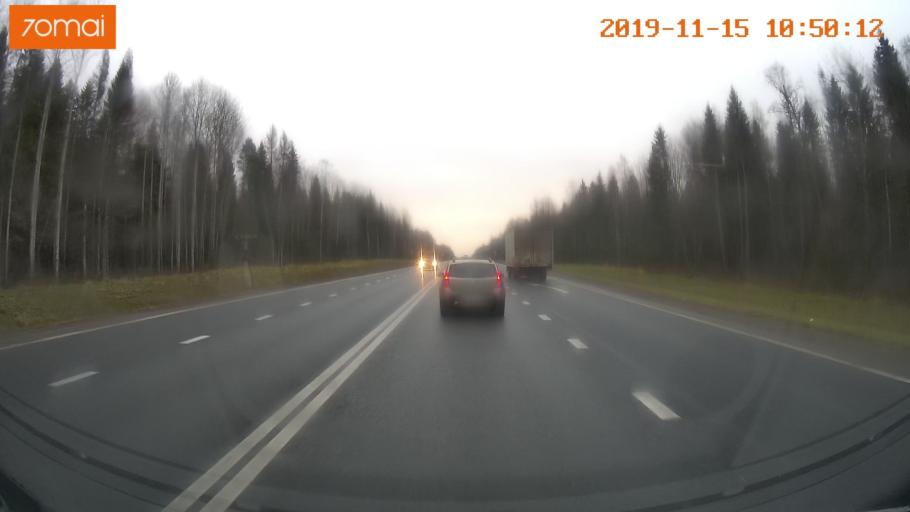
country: RU
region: Vologda
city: Chebsara
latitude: 59.1867
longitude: 38.6753
